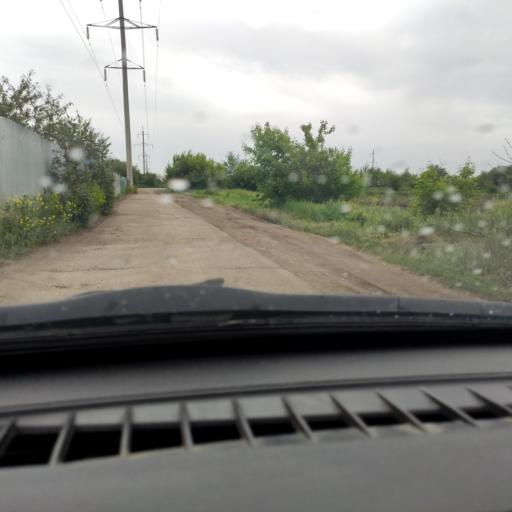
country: RU
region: Samara
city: Tol'yatti
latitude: 53.5879
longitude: 49.4354
